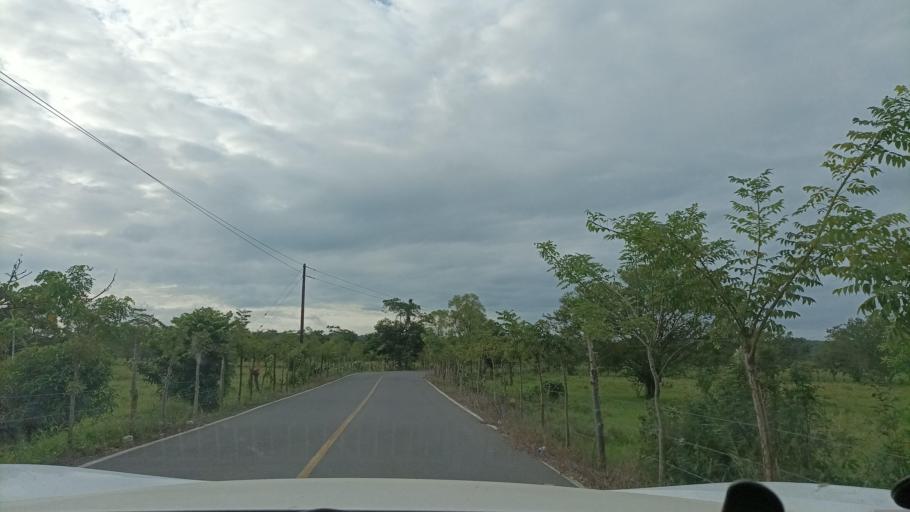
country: MX
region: Veracruz
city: Hidalgotitlan
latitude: 17.7365
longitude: -94.4876
